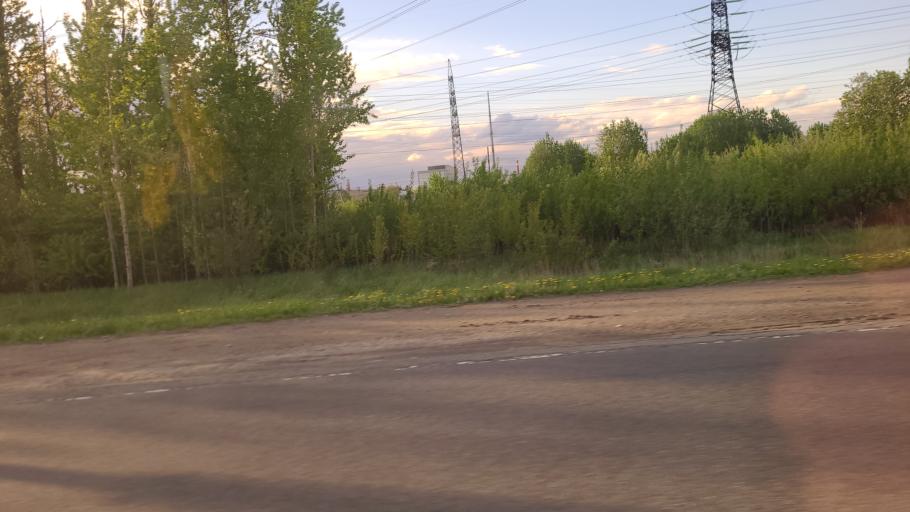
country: RU
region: St.-Petersburg
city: Kolpino
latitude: 59.7491
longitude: 30.5443
